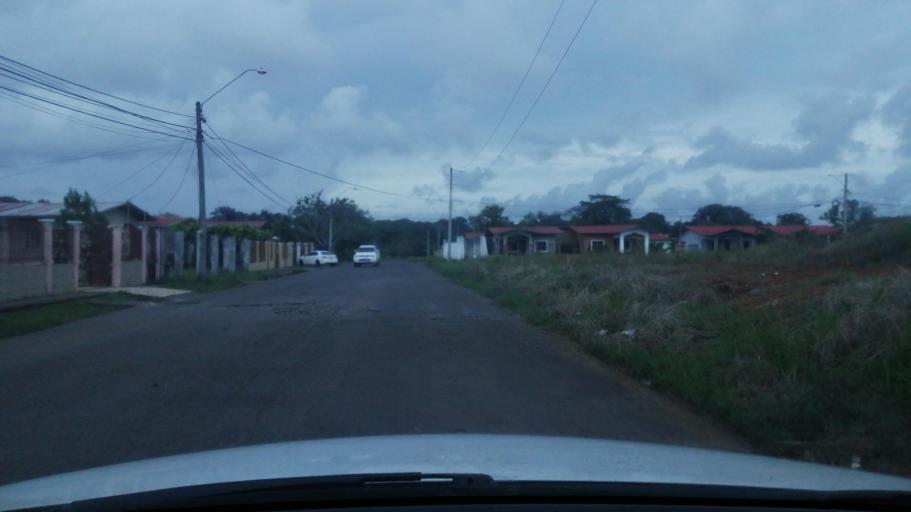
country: PA
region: Chiriqui
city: David
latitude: 8.4030
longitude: -82.4477
